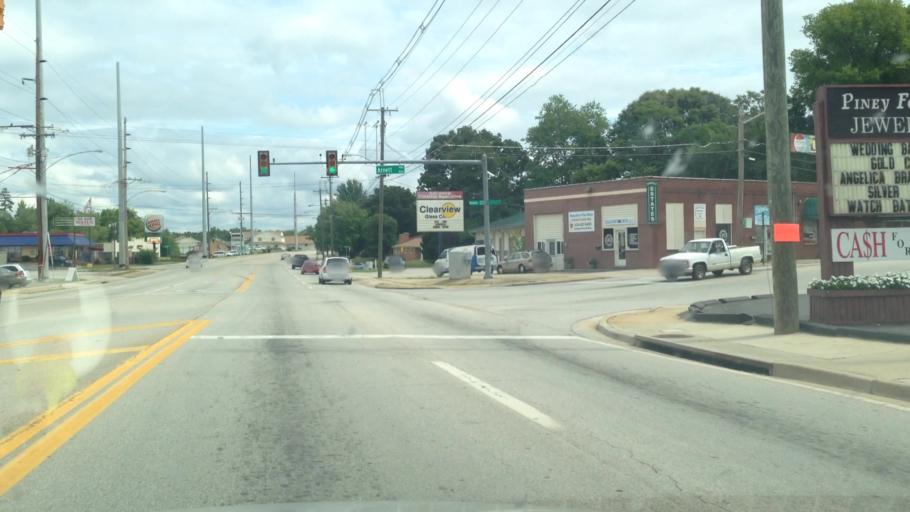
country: US
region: Virginia
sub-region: City of Danville
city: Danville
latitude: 36.6234
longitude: -79.4040
